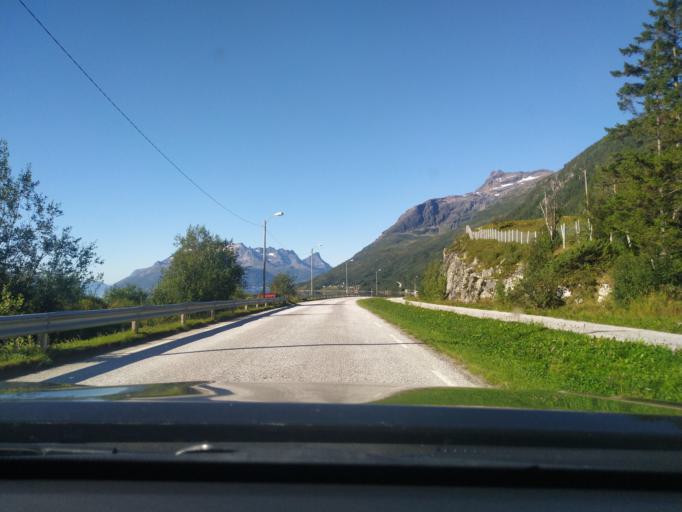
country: NO
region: Troms
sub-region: Salangen
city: Sjovegan
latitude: 68.9336
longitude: 17.7089
